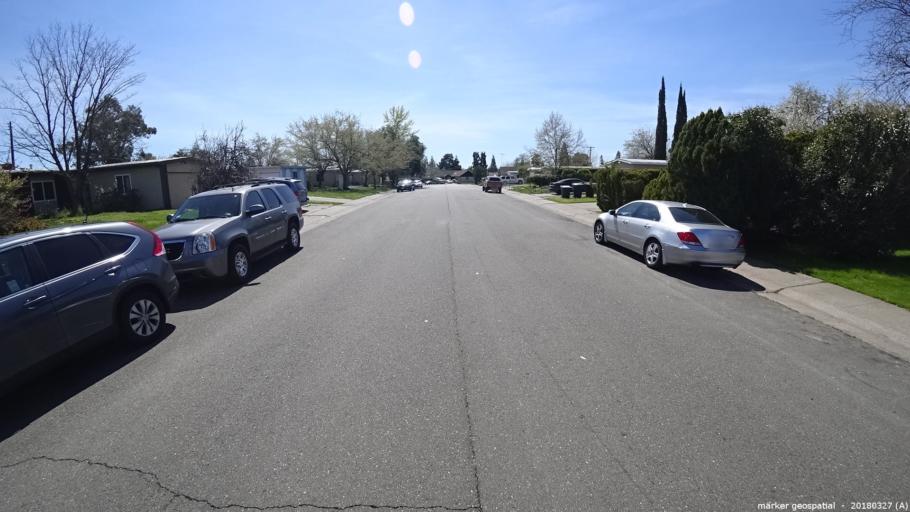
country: US
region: California
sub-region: Sacramento County
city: La Riviera
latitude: 38.5506
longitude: -121.3397
